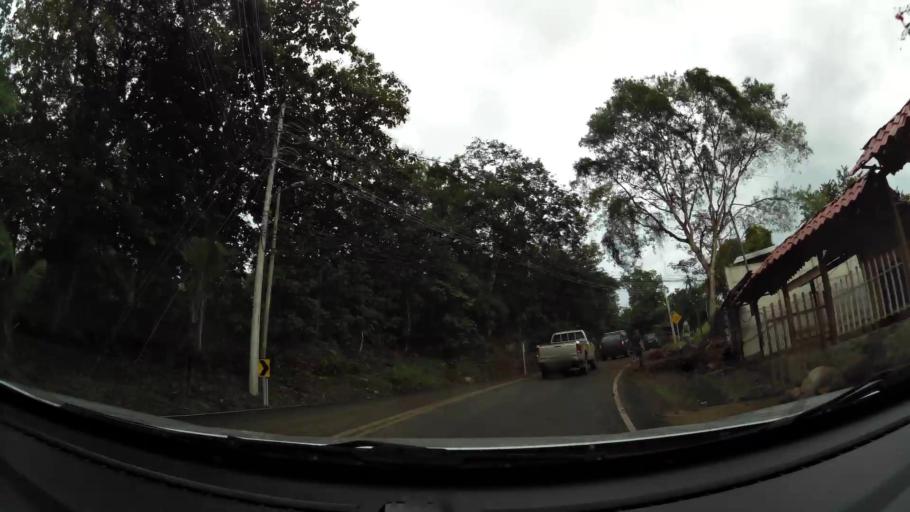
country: CR
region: Puntarenas
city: Esparza
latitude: 9.9582
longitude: -84.6023
